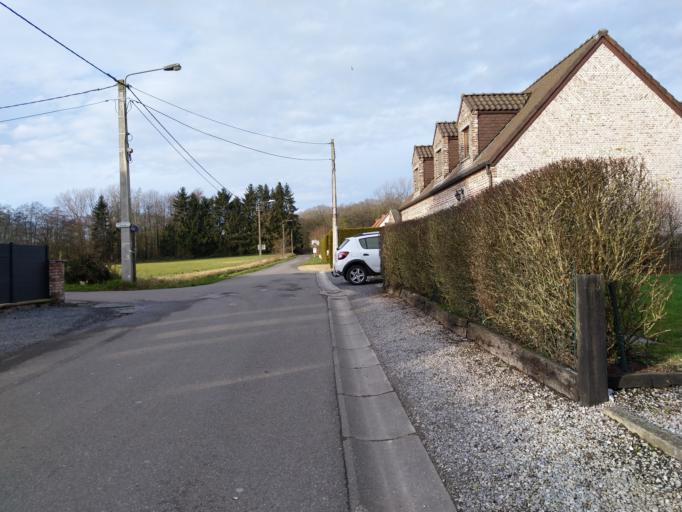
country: BE
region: Wallonia
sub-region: Province du Hainaut
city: Mons
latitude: 50.5198
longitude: 3.9892
